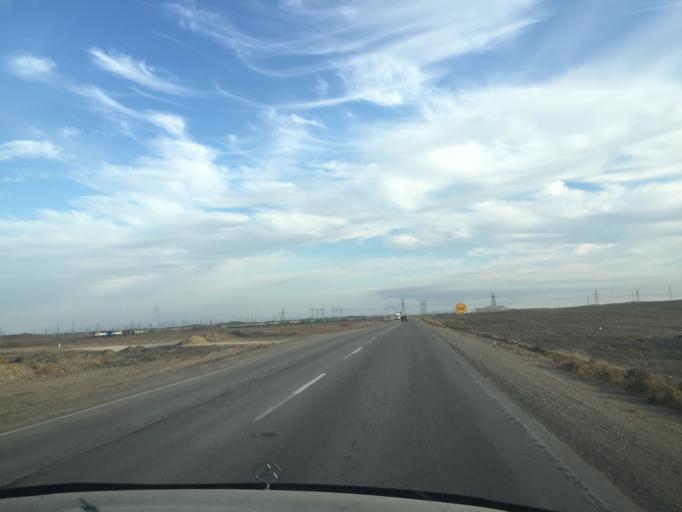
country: KZ
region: Almaty Oblysy
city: Ulken
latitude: 45.1963
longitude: 73.9036
